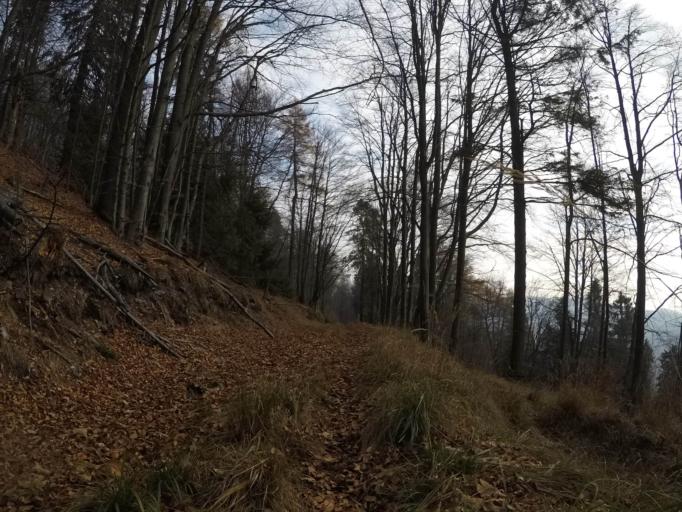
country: SK
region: Kosicky
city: Gelnica
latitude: 48.7738
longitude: 20.9544
